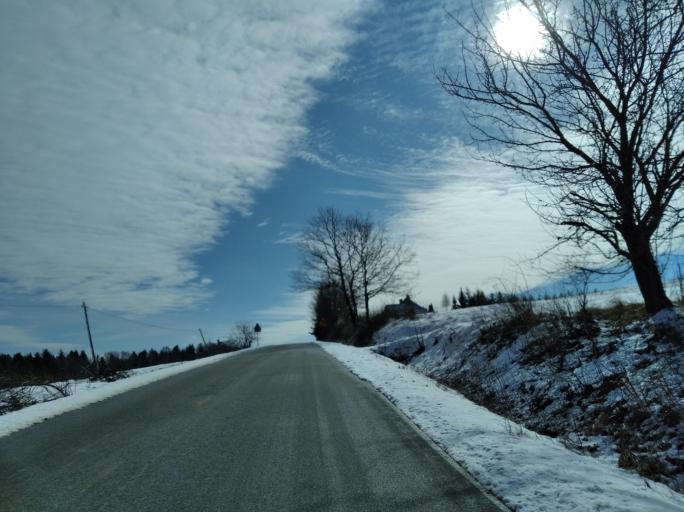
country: PL
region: Subcarpathian Voivodeship
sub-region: Powiat brzozowski
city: Jablonica Polska
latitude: 49.7277
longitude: 21.9002
